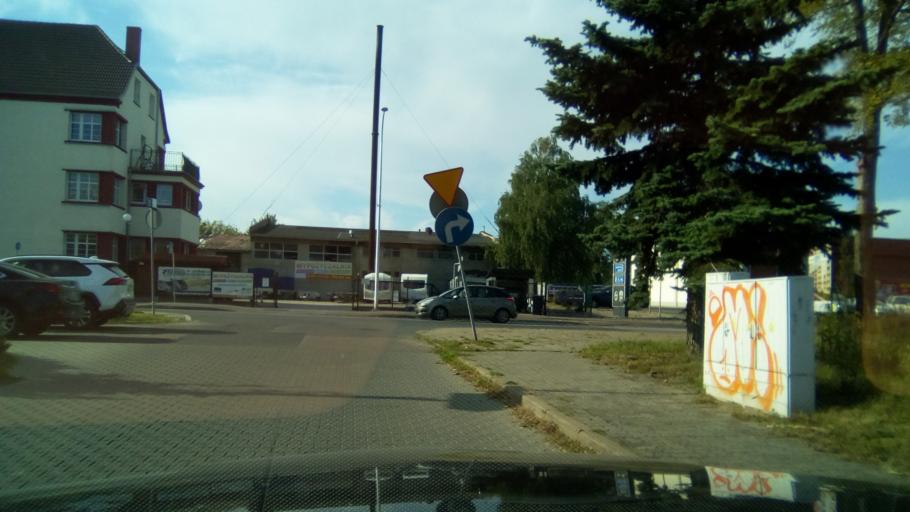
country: PL
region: Greater Poland Voivodeship
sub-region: Powiat pilski
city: Pila
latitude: 53.1443
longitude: 16.7347
